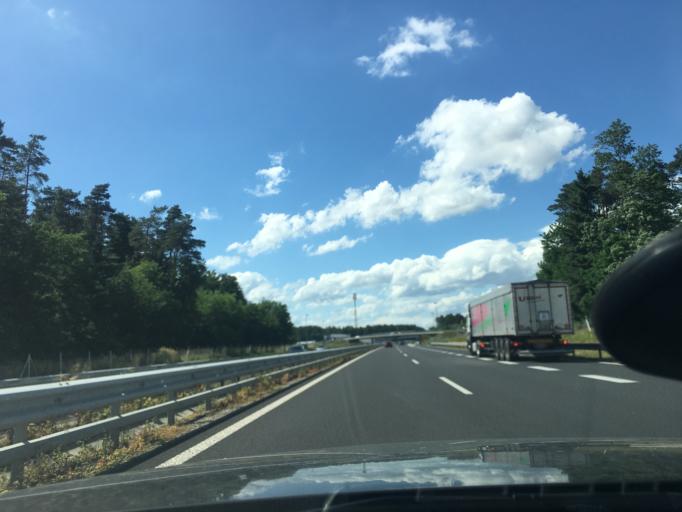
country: SI
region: Kidricevo
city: Kidricevo
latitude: 46.4095
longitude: 15.8146
